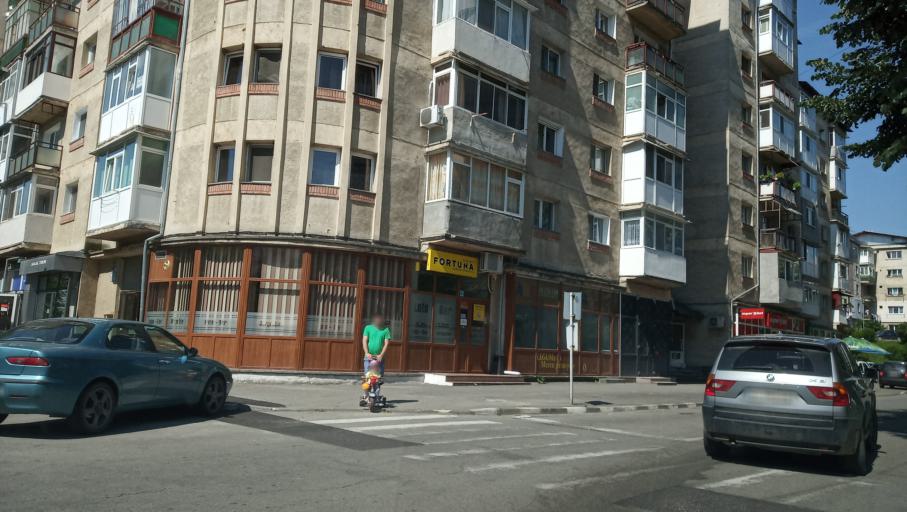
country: RO
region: Valcea
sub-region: Municipiul Ramnicu Valcea
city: Ramnicu Valcea
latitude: 45.0915
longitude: 24.3676
